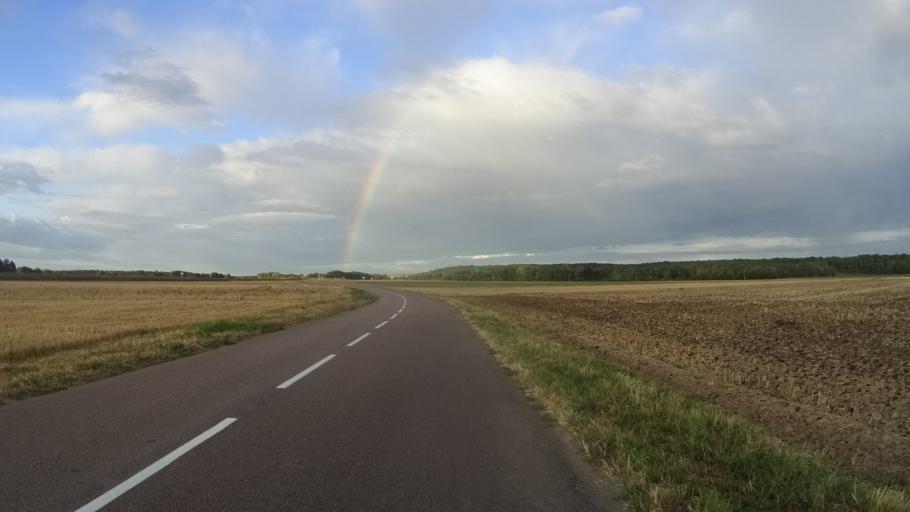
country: FR
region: Bourgogne
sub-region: Departement de la Cote-d'Or
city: Seurre
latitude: 46.9699
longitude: 5.0865
